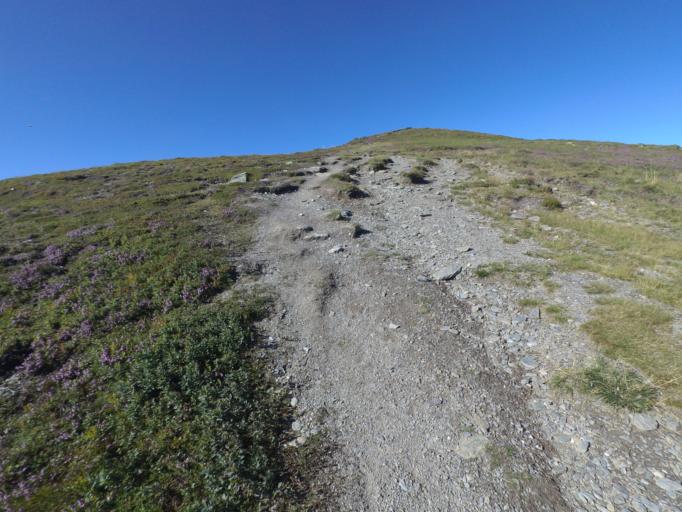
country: AT
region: Salzburg
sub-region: Politischer Bezirk Sankt Johann im Pongau
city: Goldegg
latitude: 47.3669
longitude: 13.0711
